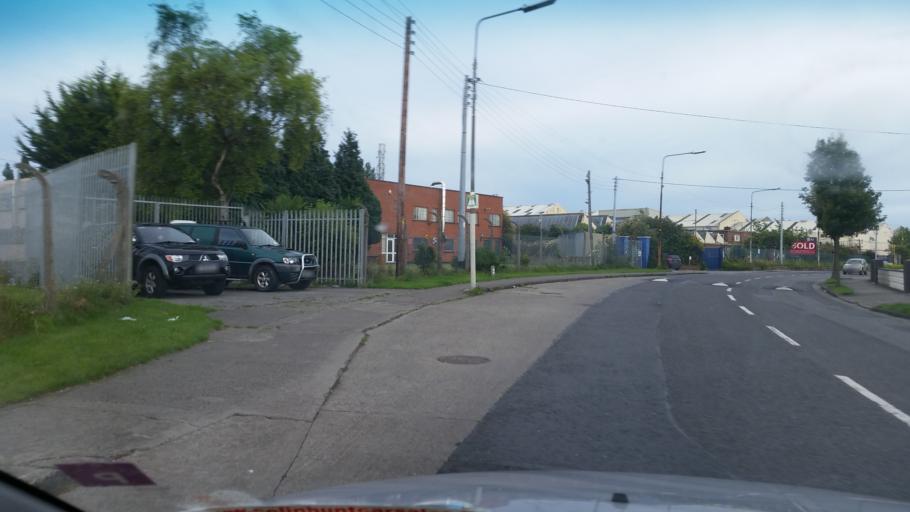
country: IE
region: Leinster
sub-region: Dublin City
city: Finglas
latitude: 53.3959
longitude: -6.3023
